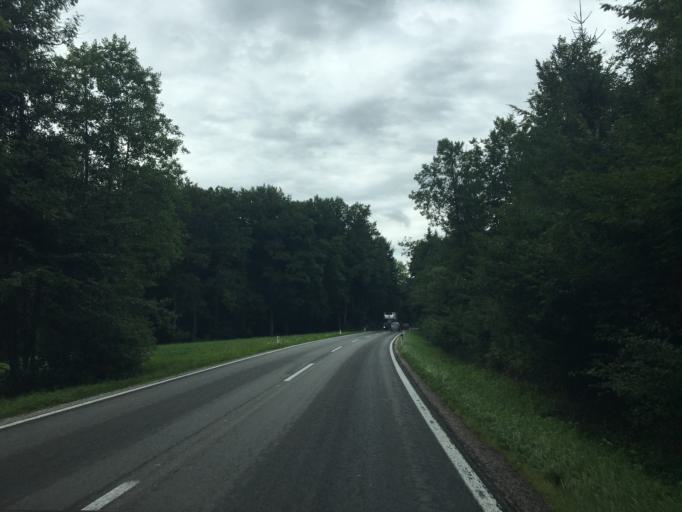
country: AT
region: Salzburg
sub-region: Politischer Bezirk Salzburg-Umgebung
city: Dorfbeuern
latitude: 48.0253
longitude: 12.9722
